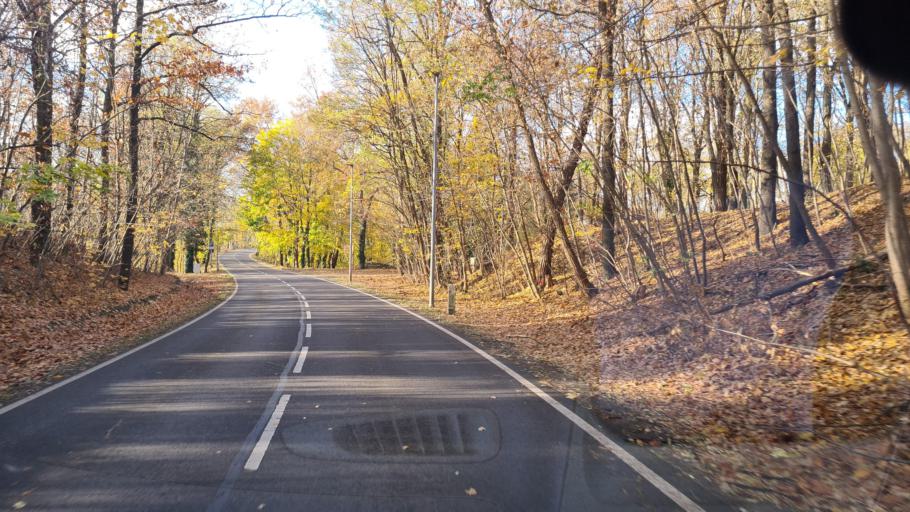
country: DE
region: Brandenburg
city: Spremberg
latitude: 51.5775
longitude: 14.3545
